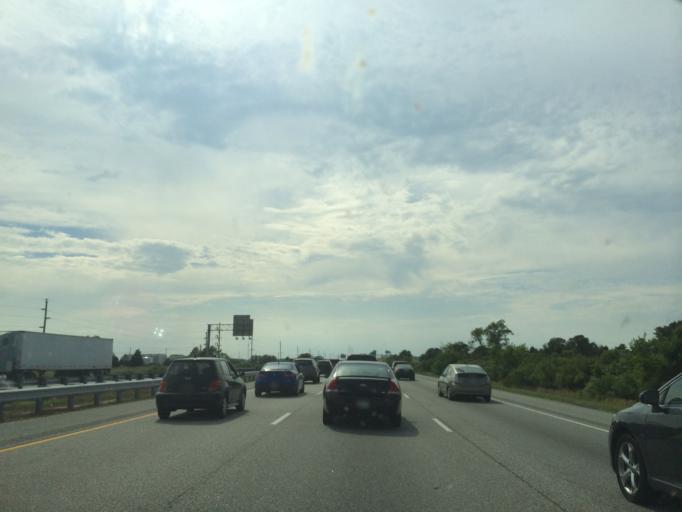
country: US
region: Maryland
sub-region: Queen Anne's County
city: Grasonville
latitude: 38.9669
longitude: -76.2306
